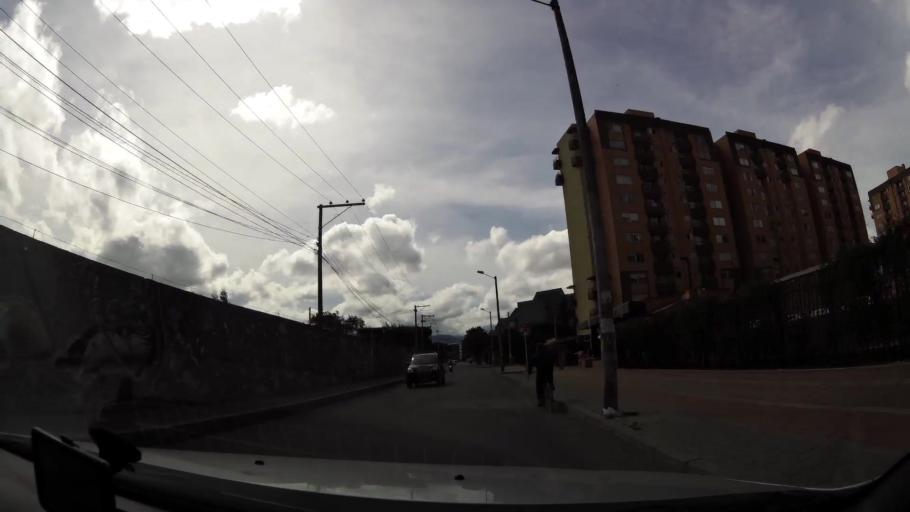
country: CO
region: Bogota D.C.
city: Bogota
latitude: 4.6452
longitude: -74.1433
